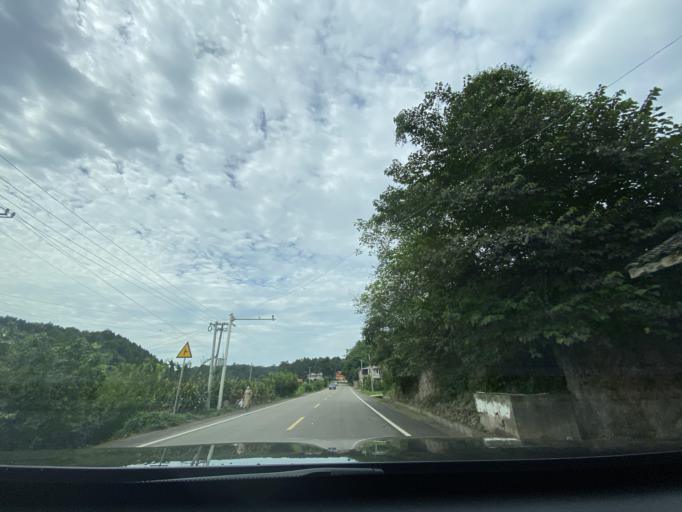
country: CN
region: Sichuan
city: Jiancheng
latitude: 30.4720
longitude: 104.6297
